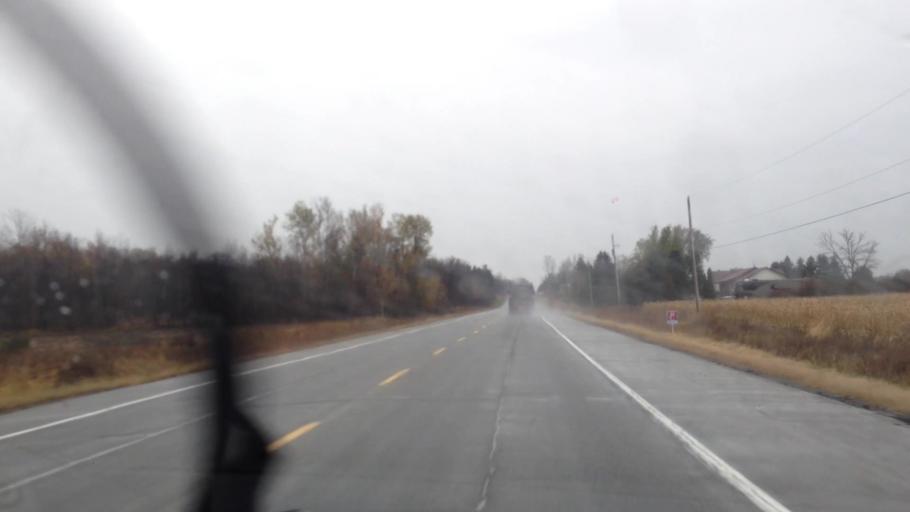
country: CA
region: Ontario
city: Clarence-Rockland
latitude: 45.3832
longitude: -75.3861
